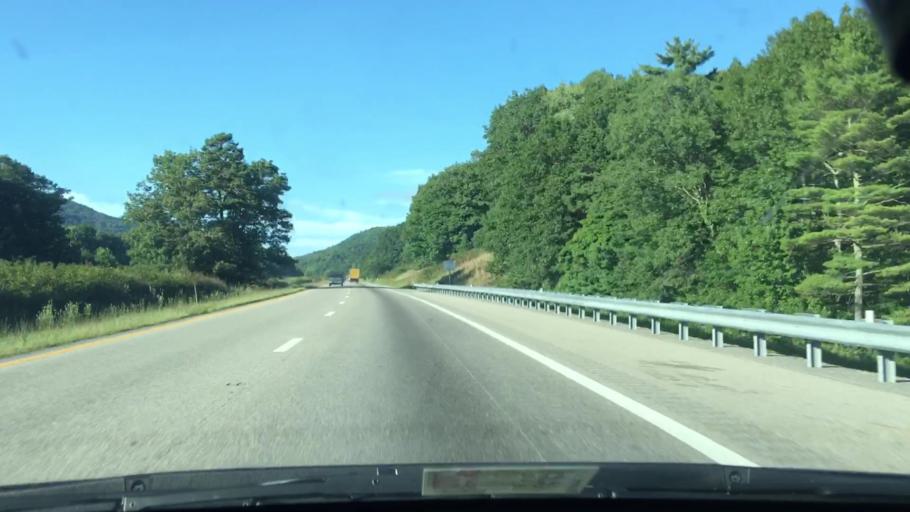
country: US
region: Virginia
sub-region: Alleghany County
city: Clifton Forge
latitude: 37.8513
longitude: -79.6306
